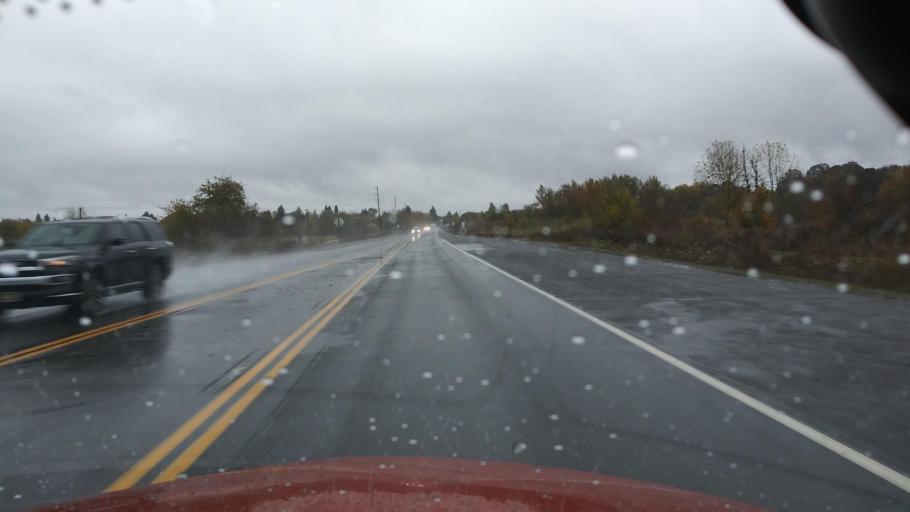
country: US
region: Oregon
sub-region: Washington County
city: Forest Grove
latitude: 45.5029
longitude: -123.1149
